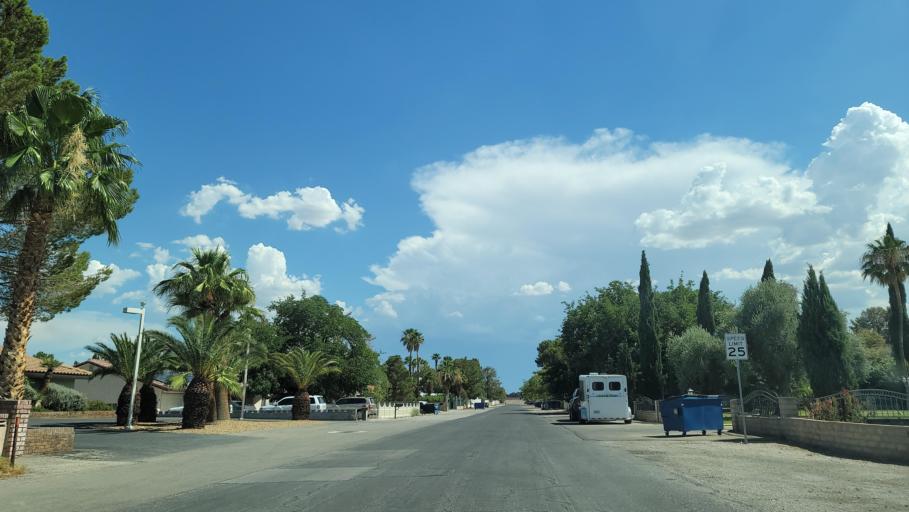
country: US
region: Nevada
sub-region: Clark County
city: Spring Valley
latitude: 36.1346
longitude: -115.2273
